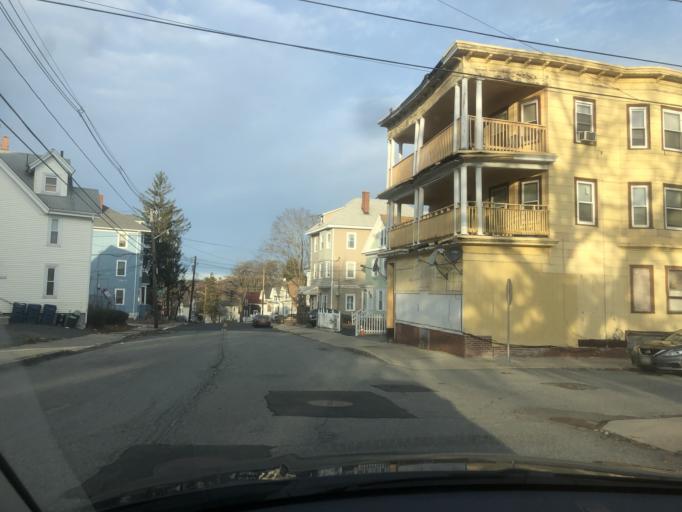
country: US
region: Massachusetts
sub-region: Essex County
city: Lawrence
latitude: 42.7210
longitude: -71.1526
